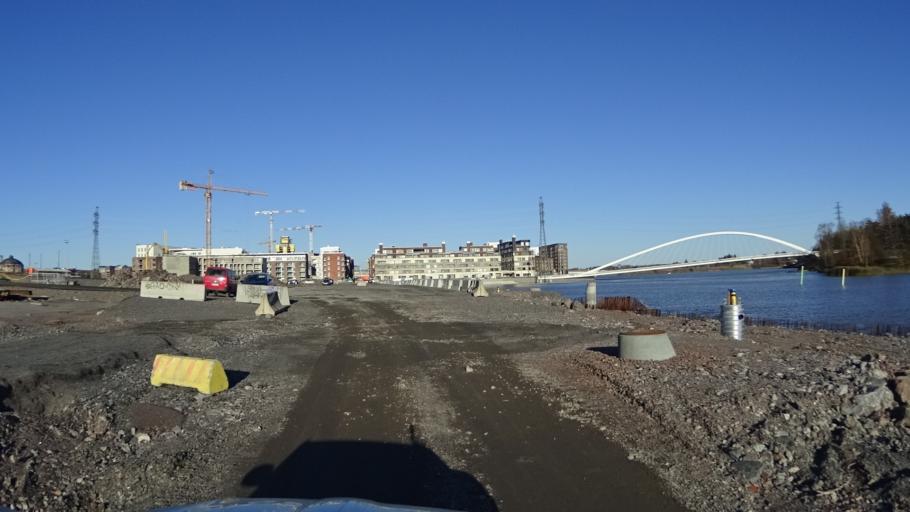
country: FI
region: Uusimaa
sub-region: Helsinki
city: Helsinki
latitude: 60.1800
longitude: 24.9784
